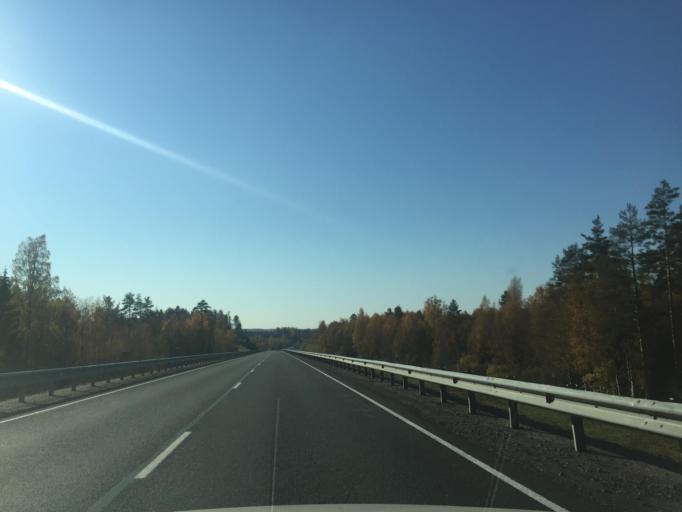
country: RU
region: Leningrad
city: Kuznechnoye
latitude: 61.3554
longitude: 29.8869
